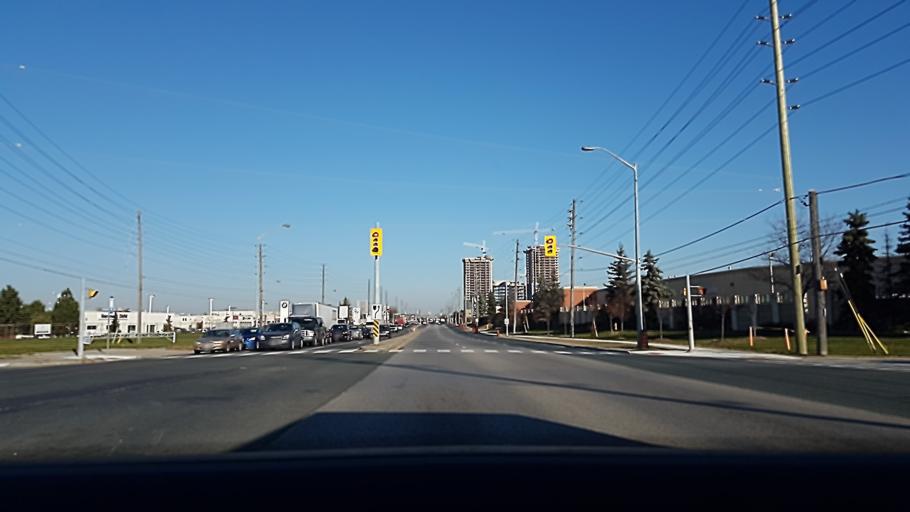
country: CA
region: Ontario
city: Concord
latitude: 43.7829
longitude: -79.5460
